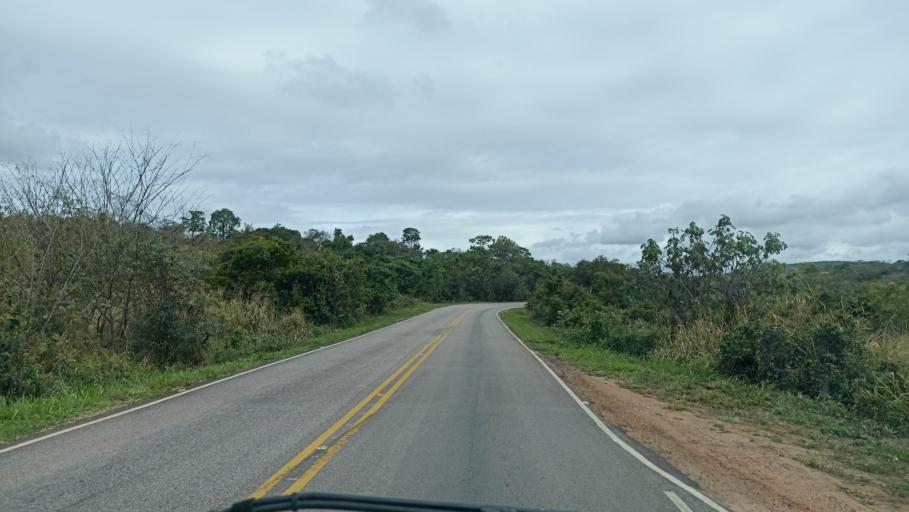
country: BR
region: Bahia
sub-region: Andarai
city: Vera Cruz
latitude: -12.9247
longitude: -41.2336
